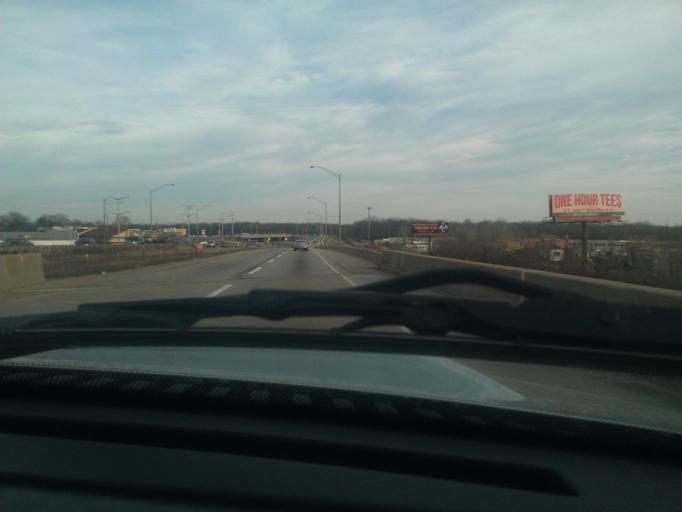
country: US
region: Illinois
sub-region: Cook County
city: Northbrook
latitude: 42.1481
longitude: -87.8387
